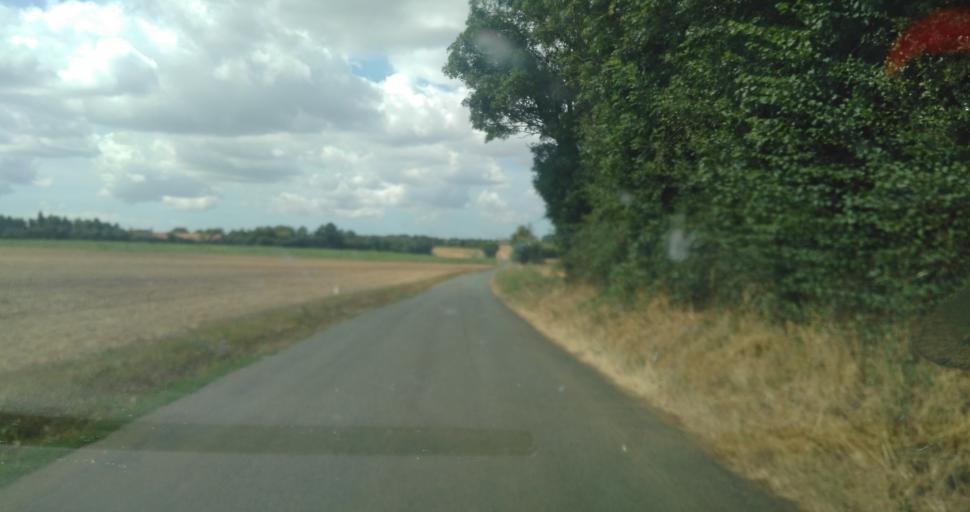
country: FR
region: Pays de la Loire
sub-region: Departement de la Vendee
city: Sainte-Hermine
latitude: 46.5311
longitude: -1.0879
